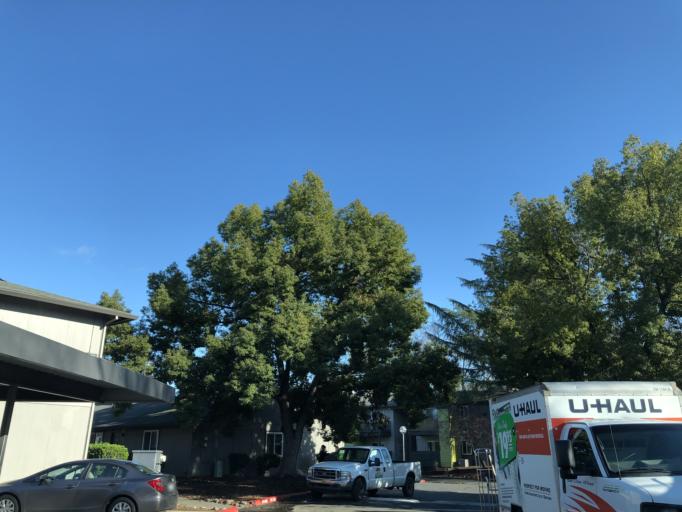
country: US
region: California
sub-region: Sacramento County
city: Rosemont
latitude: 38.5526
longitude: -121.4062
